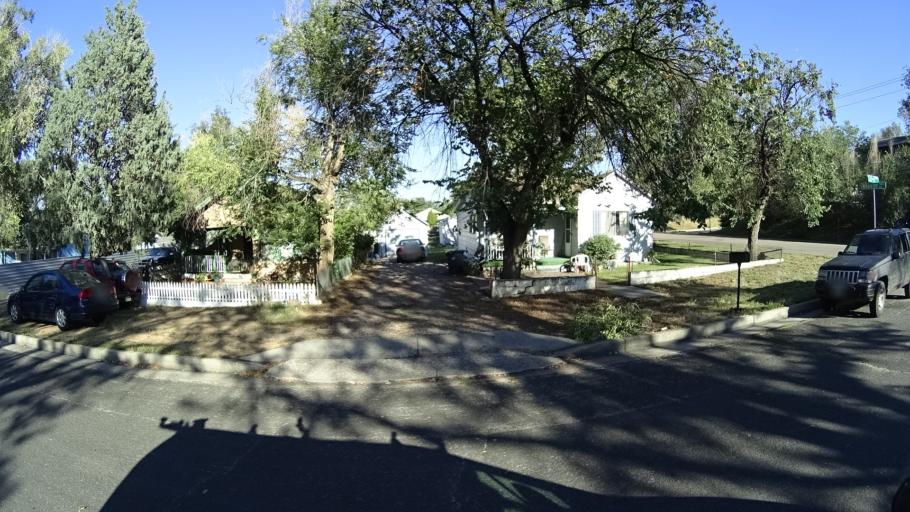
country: US
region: Colorado
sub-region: El Paso County
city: Colorado Springs
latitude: 38.8356
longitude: -104.8691
